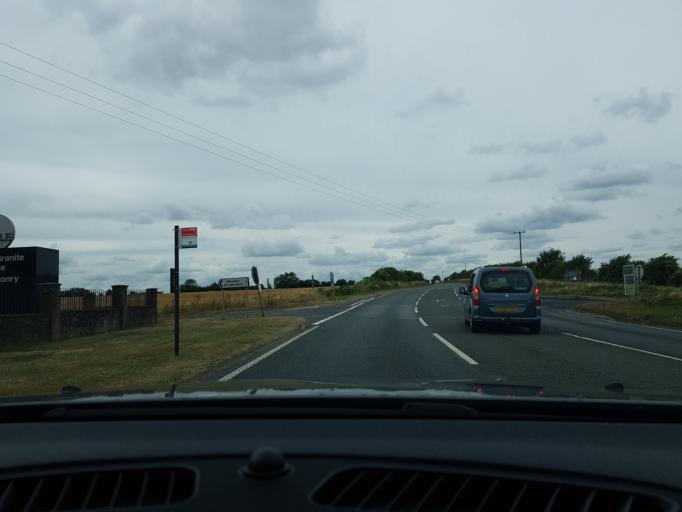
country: GB
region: England
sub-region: Hampshire
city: Basingstoke
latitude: 51.2865
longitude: -1.1395
